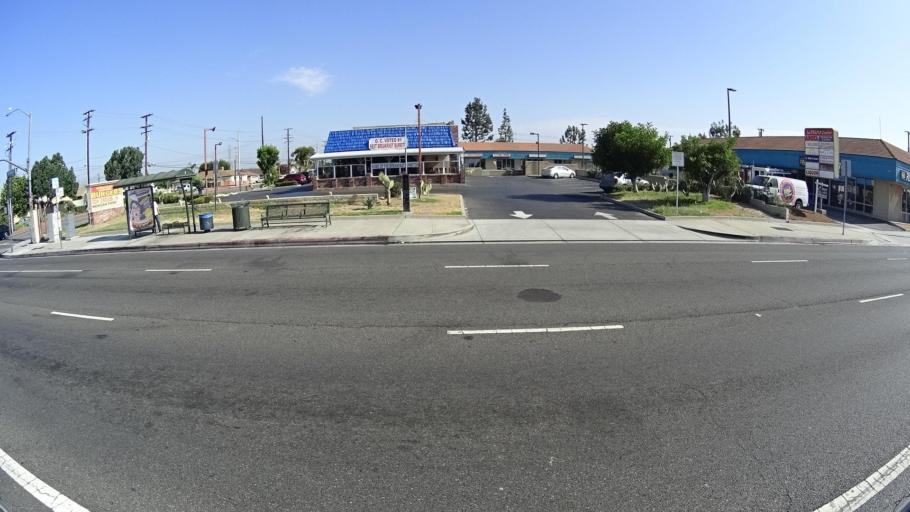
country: US
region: California
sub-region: Orange County
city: Buena Park
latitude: 33.8473
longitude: -117.9841
